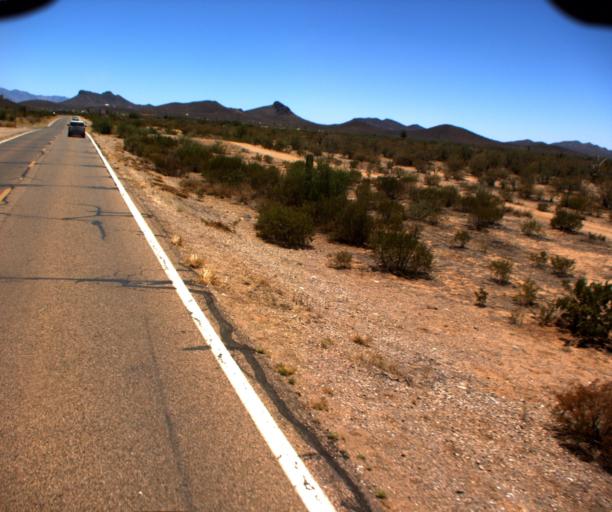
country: US
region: Arizona
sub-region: Pima County
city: Sells
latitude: 31.9281
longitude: -111.9035
